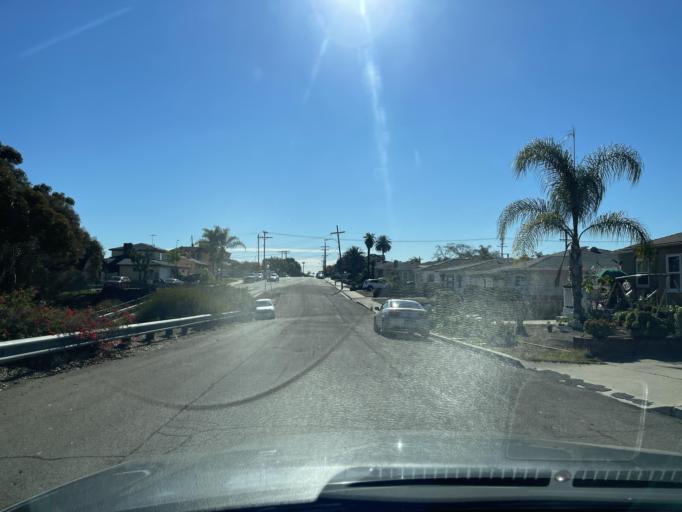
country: US
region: California
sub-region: San Diego County
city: National City
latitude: 32.6744
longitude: -117.0928
